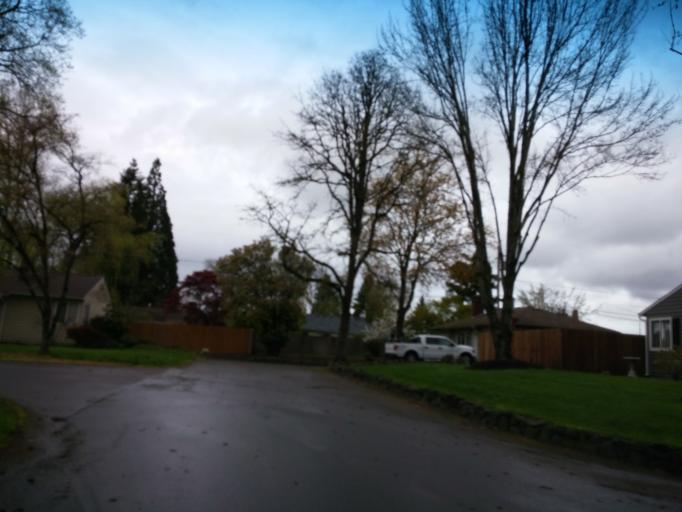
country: US
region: Oregon
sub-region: Washington County
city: Cedar Mill
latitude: 45.5192
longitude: -122.8179
